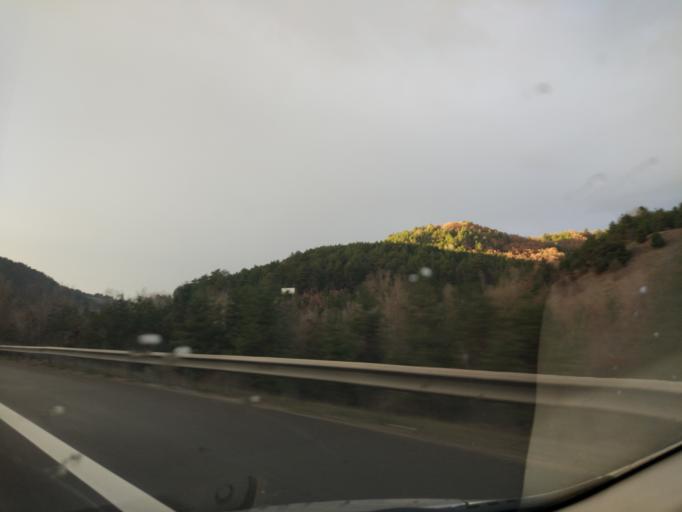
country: TR
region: Bolu
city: Bolu
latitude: 40.7404
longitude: 31.7894
